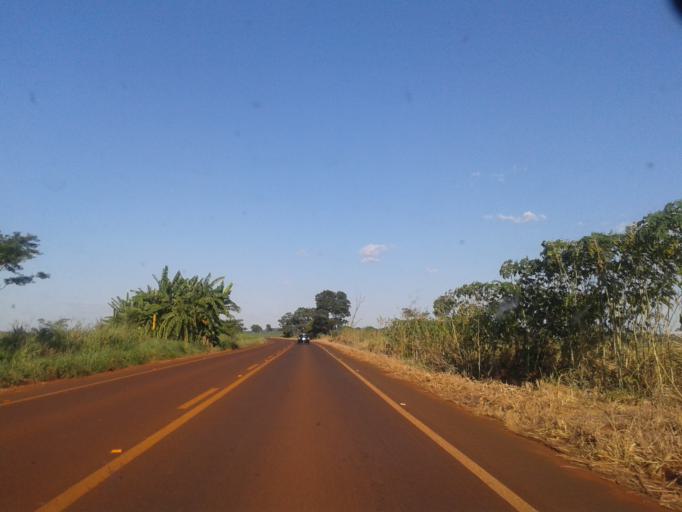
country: BR
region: Minas Gerais
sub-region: Capinopolis
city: Capinopolis
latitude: -18.7114
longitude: -49.8458
